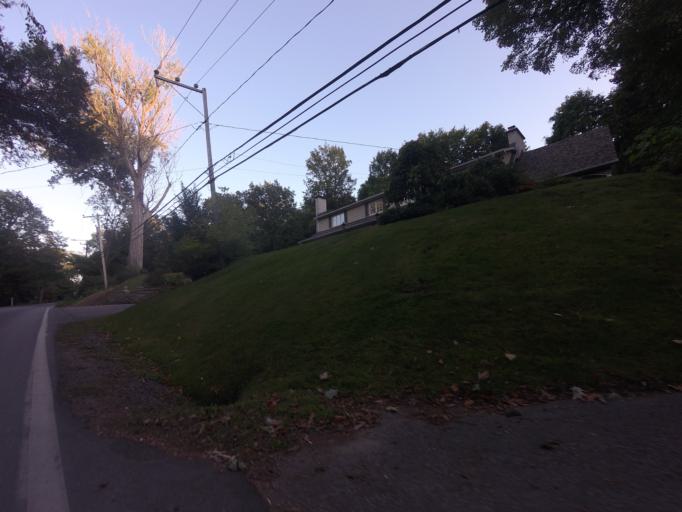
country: CA
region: Quebec
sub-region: Monteregie
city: Hudson
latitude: 45.4681
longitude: -74.1630
